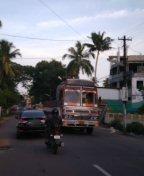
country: IN
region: Kerala
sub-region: Thrissur District
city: Trichur
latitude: 10.5271
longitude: 76.1874
